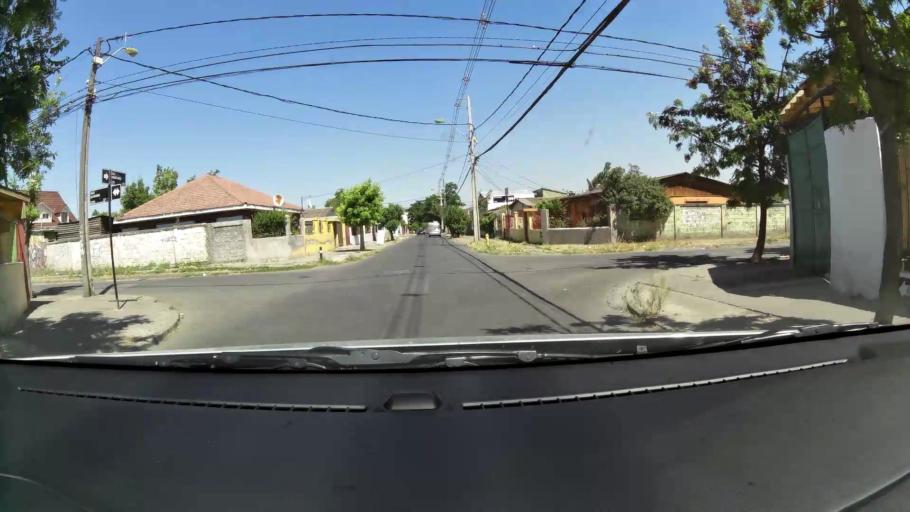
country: CL
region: Santiago Metropolitan
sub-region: Provincia de Santiago
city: La Pintana
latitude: -33.5638
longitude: -70.6610
